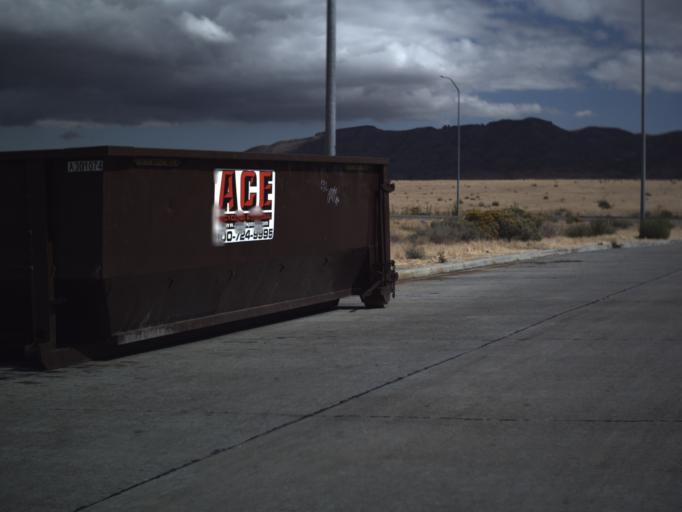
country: US
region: Utah
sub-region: Tooele County
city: Grantsville
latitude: 40.7560
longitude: -113.0185
